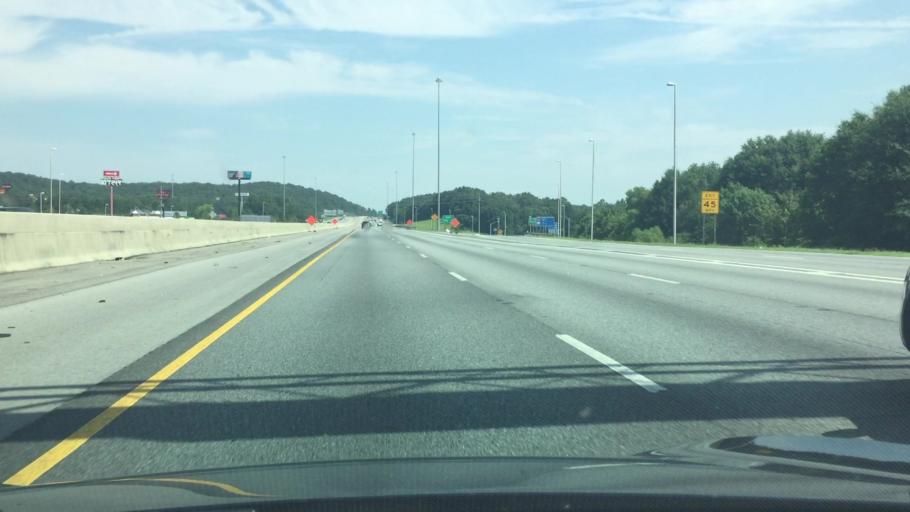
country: US
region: Alabama
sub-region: Shelby County
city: Indian Springs Village
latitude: 33.3337
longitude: -86.7794
